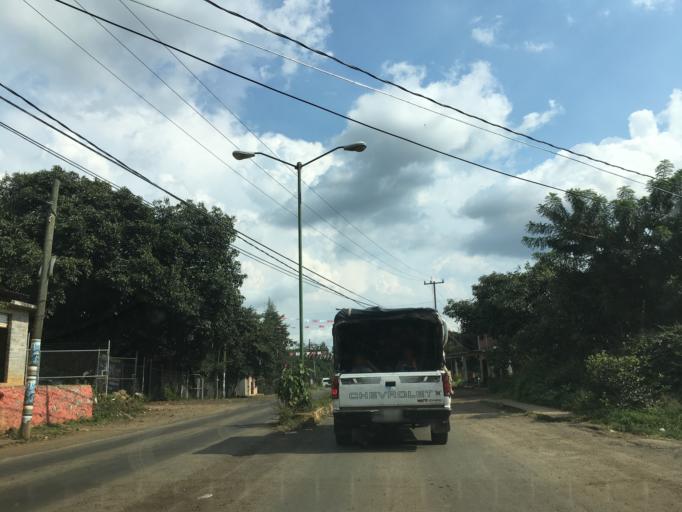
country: MX
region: Michoacan
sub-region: Ziracuaretiro
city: Patuan
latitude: 19.4432
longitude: -101.8848
